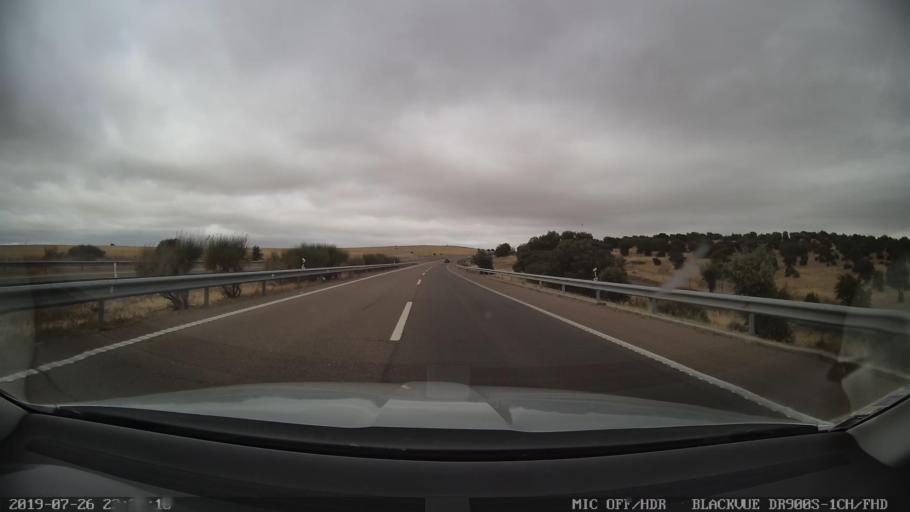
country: ES
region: Extremadura
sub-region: Provincia de Caceres
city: Santa Cruz de la Sierra
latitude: 39.3714
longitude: -5.8777
